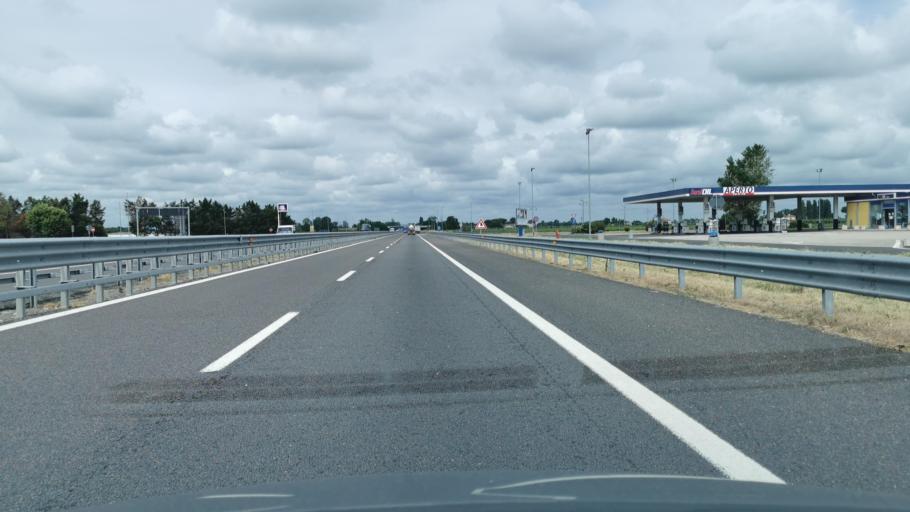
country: IT
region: Emilia-Romagna
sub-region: Provincia di Ravenna
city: Russi
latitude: 44.4025
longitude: 12.0467
